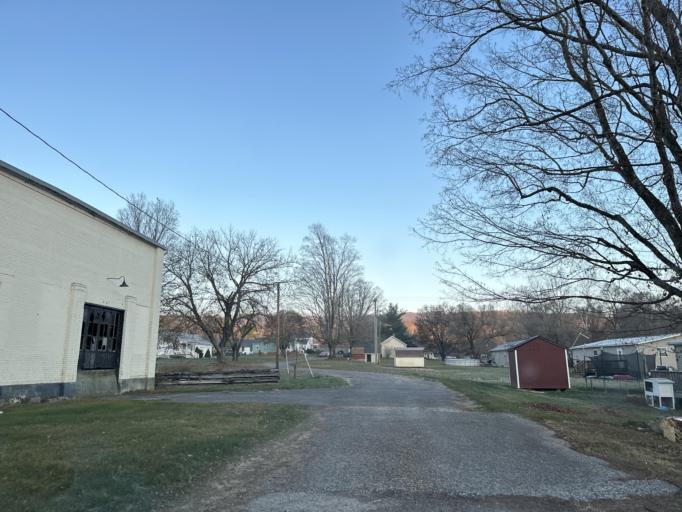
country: US
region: Virginia
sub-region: Rockbridge County
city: East Lexington
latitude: 38.0753
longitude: -79.3917
